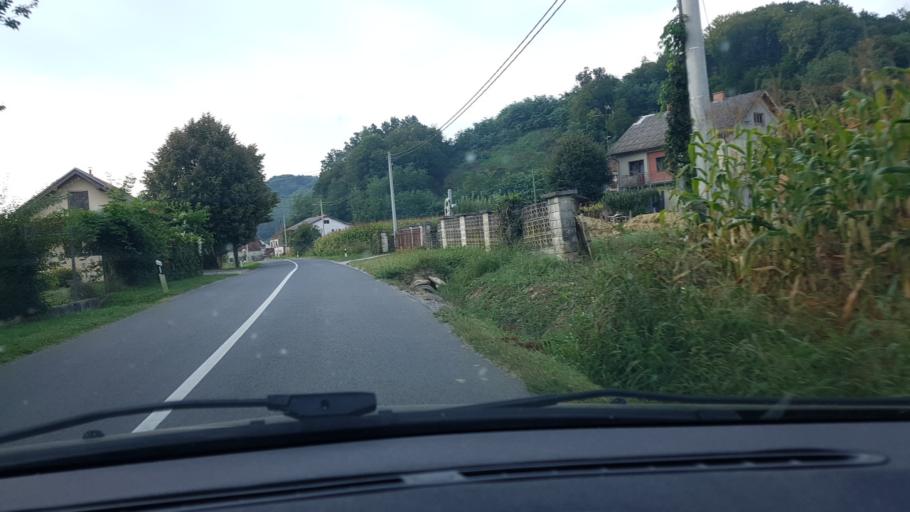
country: HR
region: Krapinsko-Zagorska
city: Mihovljan
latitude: 46.1095
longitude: 16.0108
